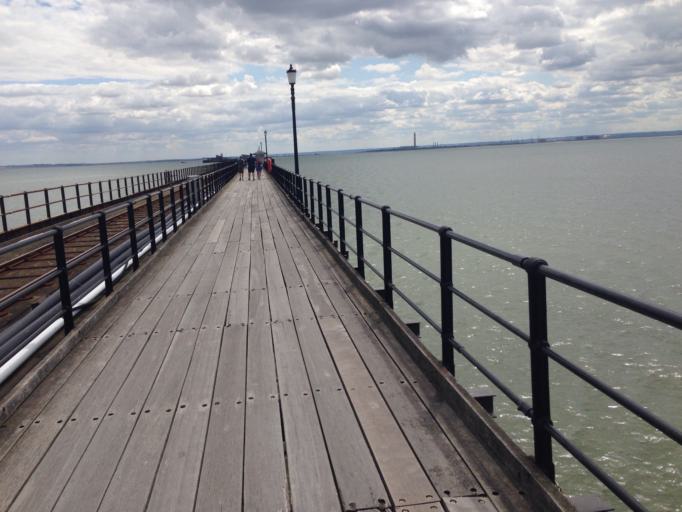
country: GB
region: England
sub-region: Southend-on-Sea
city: Southend-on-Sea
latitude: 51.5271
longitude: 0.7178
